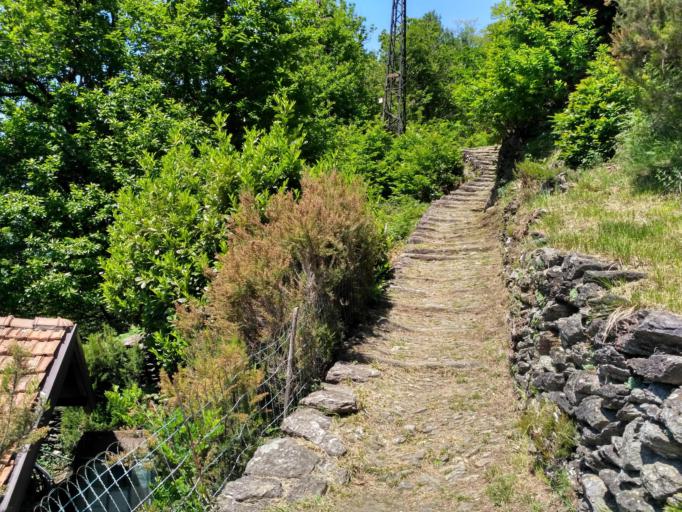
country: IT
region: Lombardy
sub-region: Provincia di Lecco
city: Dorio
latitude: 46.1053
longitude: 9.3236
